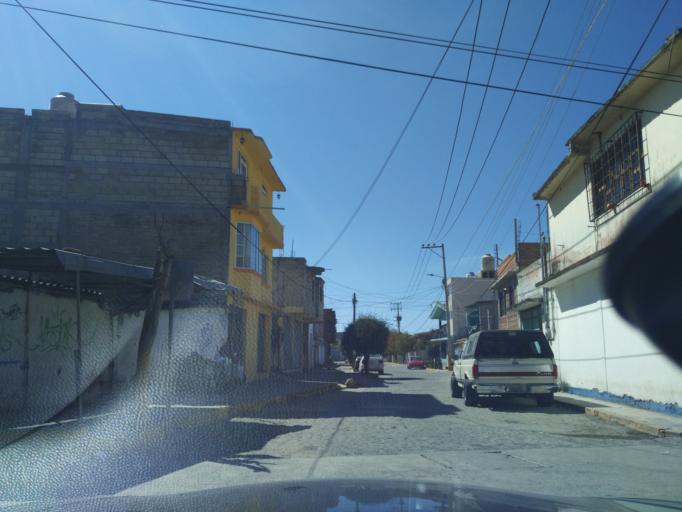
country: MX
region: Morelos
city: Ocoyoacac
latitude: 19.2697
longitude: -99.4622
